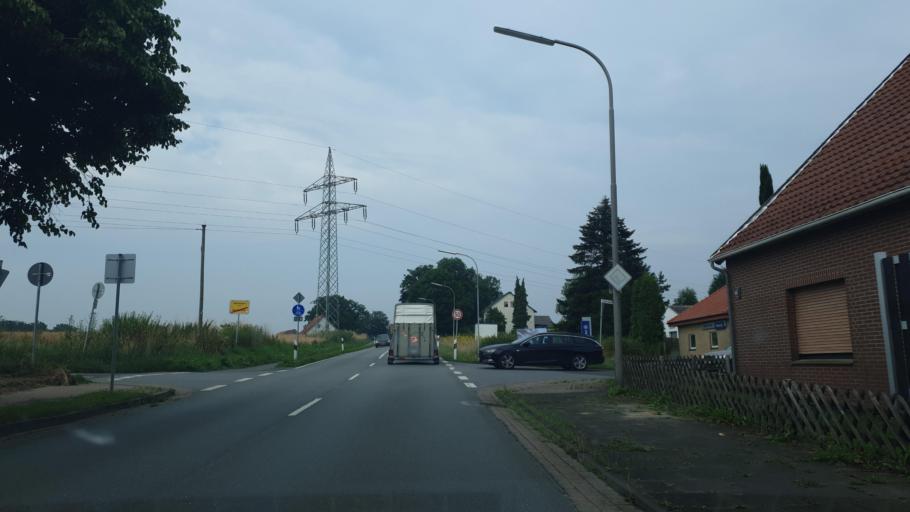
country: DE
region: North Rhine-Westphalia
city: Loehne
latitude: 52.2297
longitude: 8.7364
